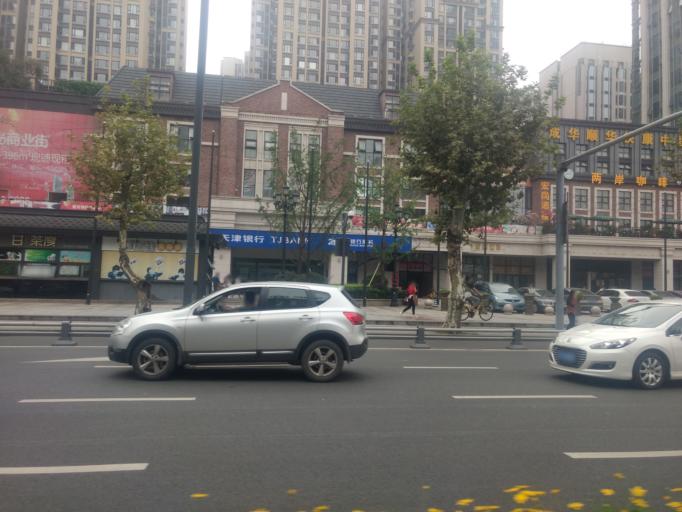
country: CN
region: Sichuan
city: Chengdu
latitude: 30.6847
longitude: 104.0968
